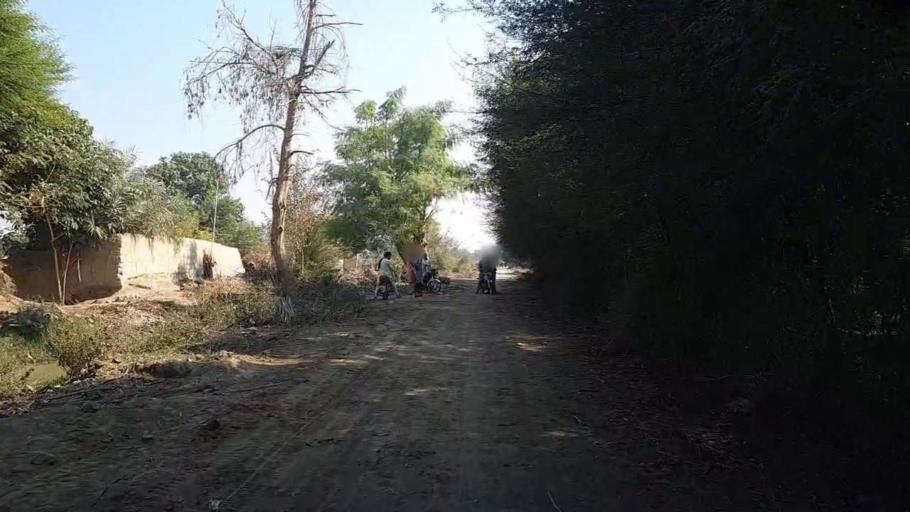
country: PK
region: Sindh
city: Bozdar
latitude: 27.1921
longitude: 68.6220
